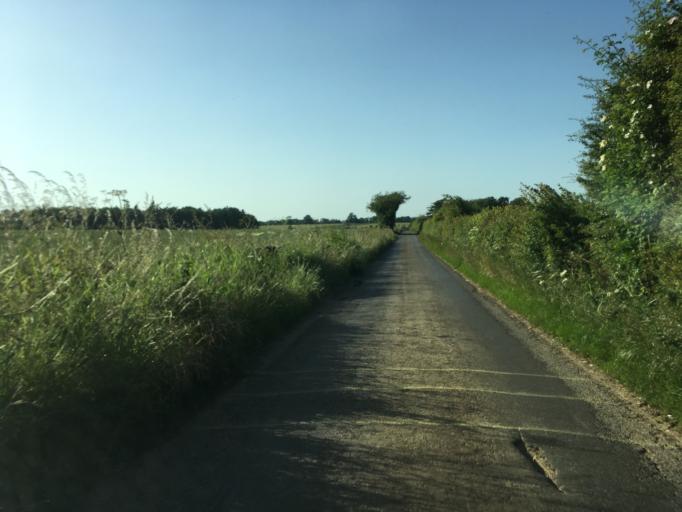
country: GB
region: England
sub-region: Oxfordshire
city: Burford
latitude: 51.7794
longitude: -1.7043
